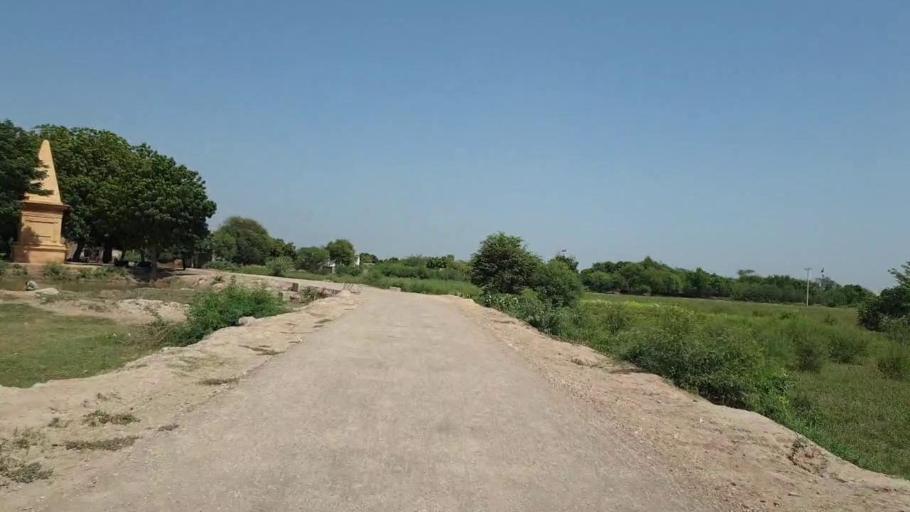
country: PK
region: Sindh
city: Hyderabad
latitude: 25.4646
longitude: 68.4282
